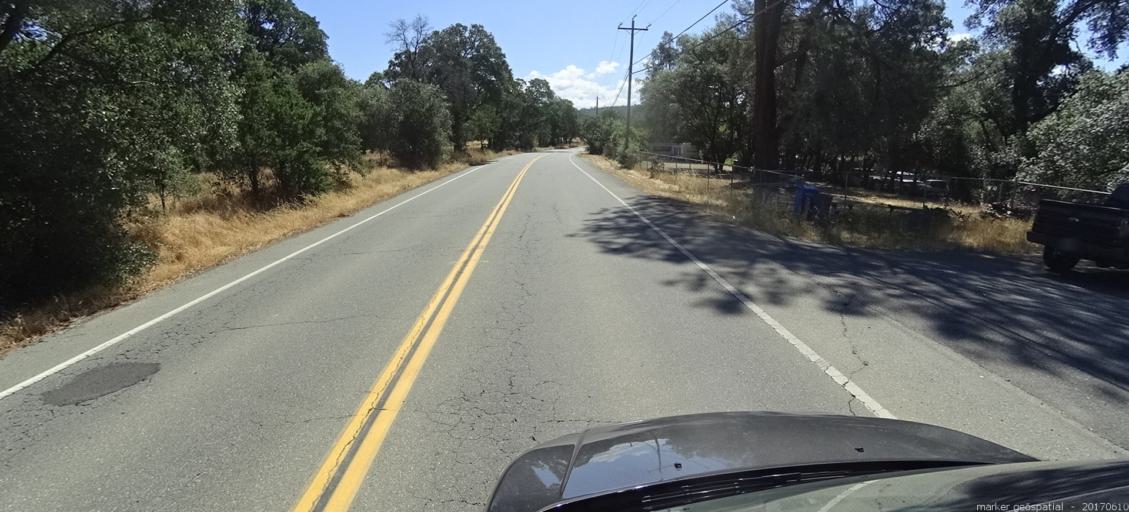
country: US
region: California
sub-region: Butte County
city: Oroville East
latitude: 39.5063
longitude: -121.5059
